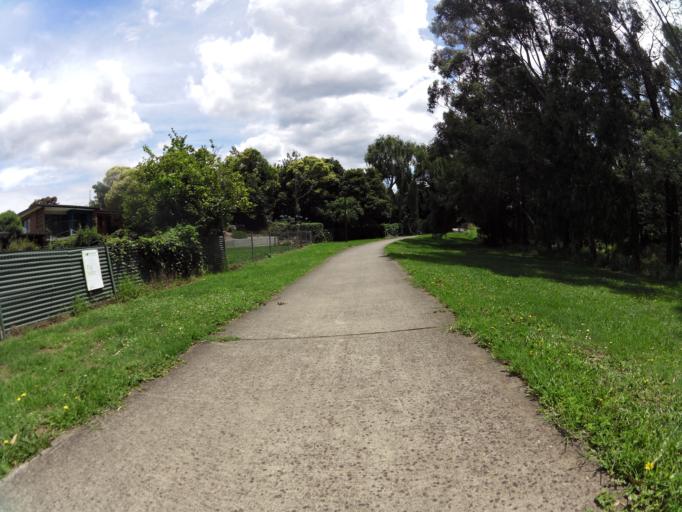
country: AU
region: Victoria
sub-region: Latrobe
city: Traralgon
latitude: -38.1911
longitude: 146.5382
